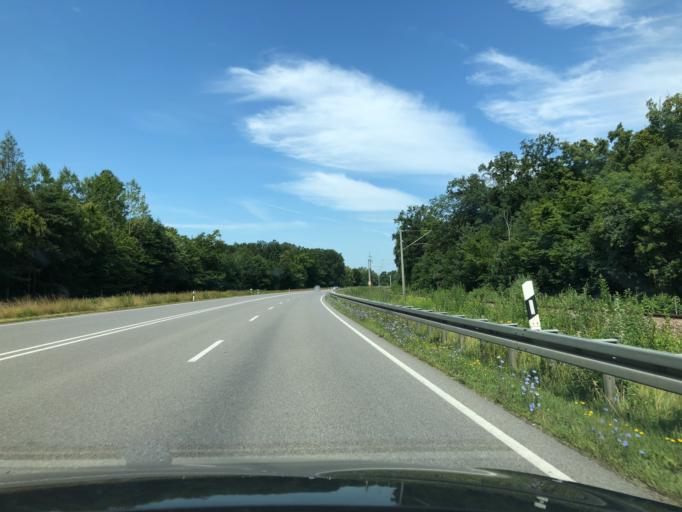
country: DE
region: Bavaria
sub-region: Upper Bavaria
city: Karlskron
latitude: 48.7072
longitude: 11.3735
